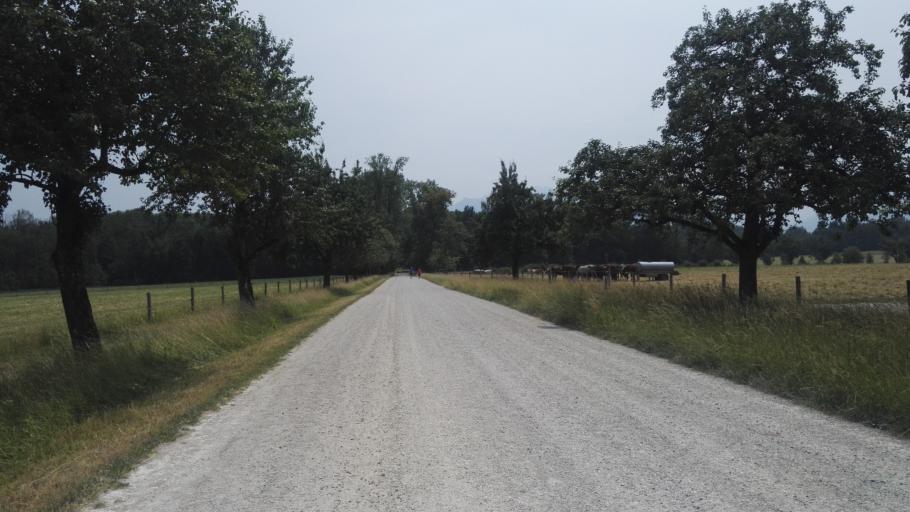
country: DE
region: Bavaria
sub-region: Upper Bavaria
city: Chiemsee
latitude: 47.8647
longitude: 12.3940
